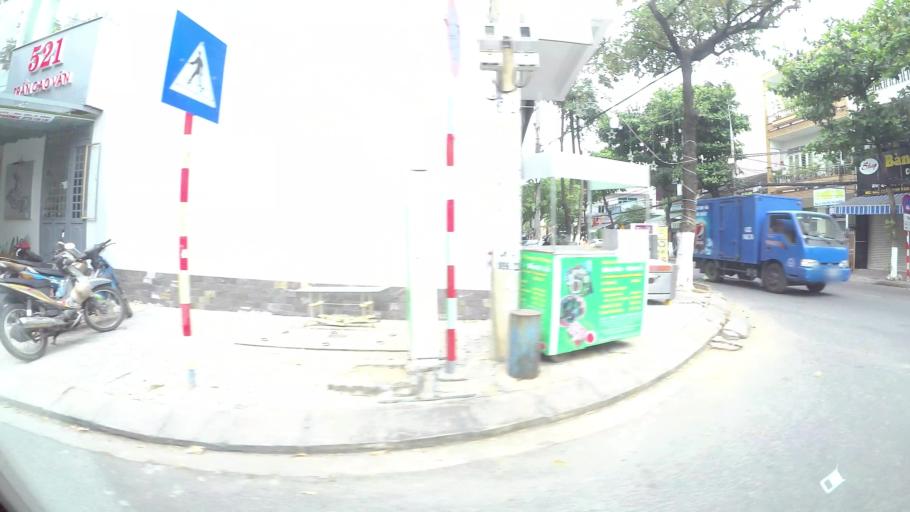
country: VN
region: Da Nang
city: Thanh Khe
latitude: 16.0713
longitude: 108.1904
